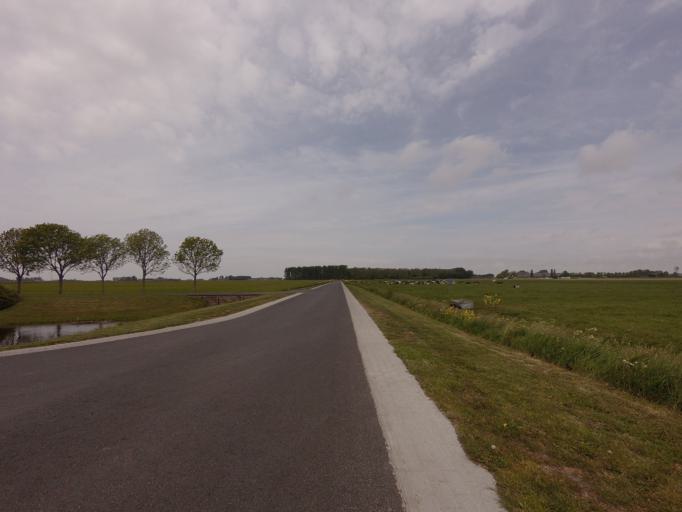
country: NL
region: Friesland
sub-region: Sudwest Fryslan
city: Bolsward
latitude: 53.0902
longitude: 5.4803
